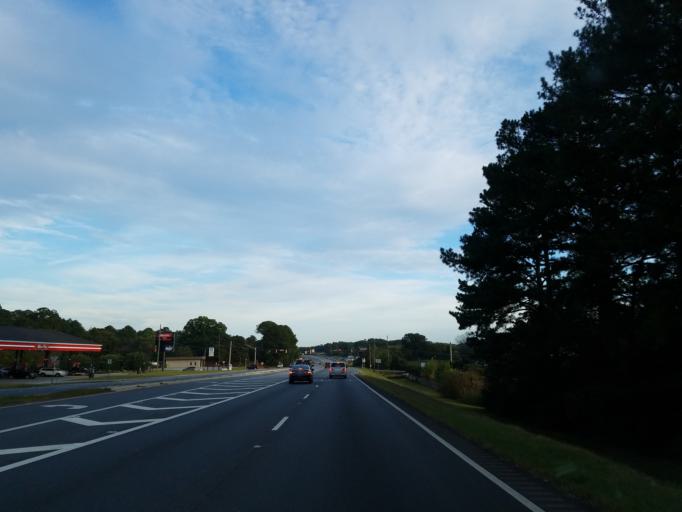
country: US
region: Georgia
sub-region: Bartow County
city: Cartersville
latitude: 34.2144
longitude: -84.8354
